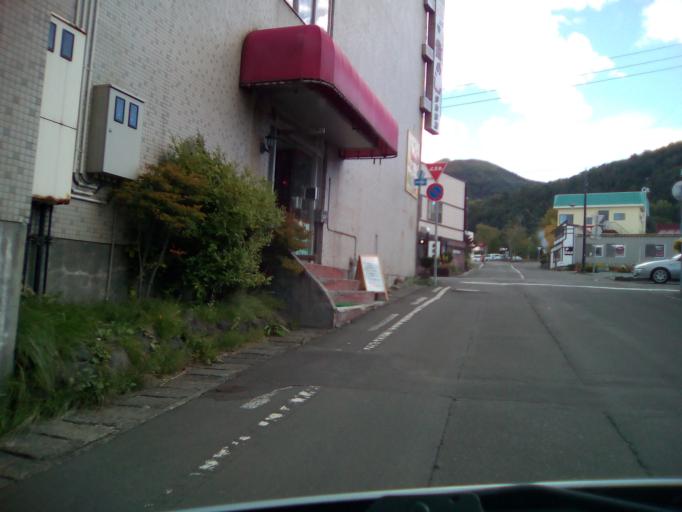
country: JP
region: Hokkaido
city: Date
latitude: 42.5656
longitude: 140.8182
